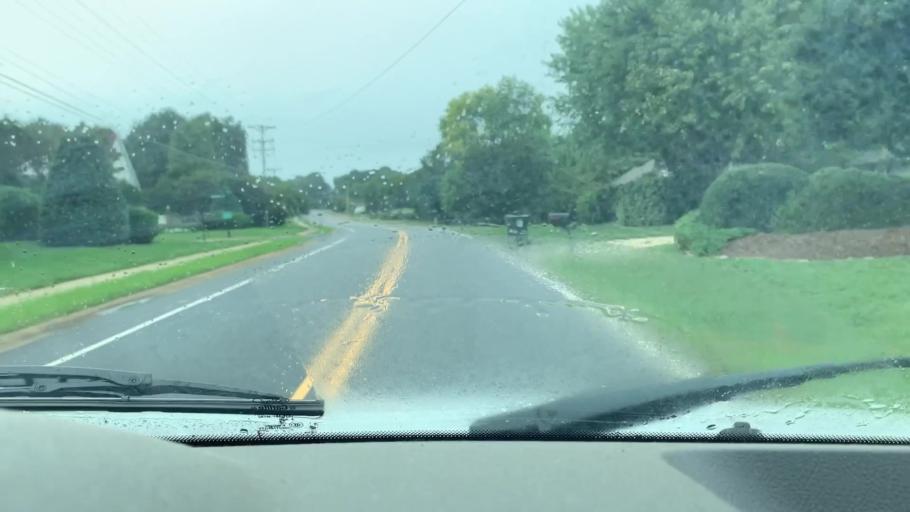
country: US
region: North Carolina
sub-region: Mecklenburg County
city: Cornelius
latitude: 35.4849
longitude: -80.8963
